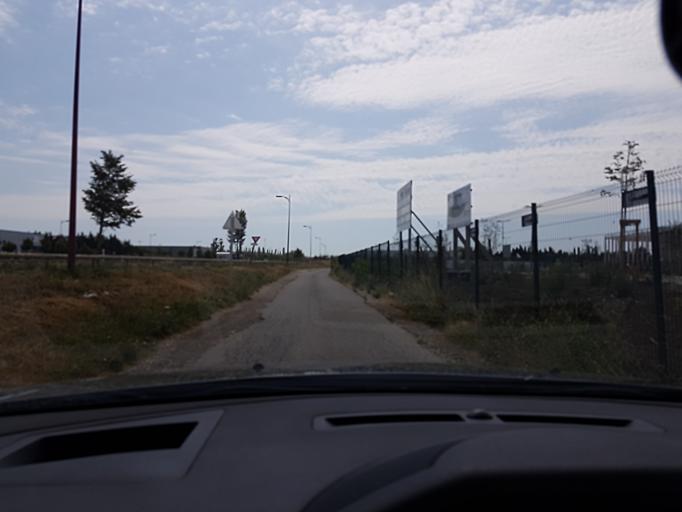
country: FR
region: Provence-Alpes-Cote d'Azur
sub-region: Departement du Vaucluse
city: Entraigues-sur-la-Sorgue
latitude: 43.9877
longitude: 4.9272
